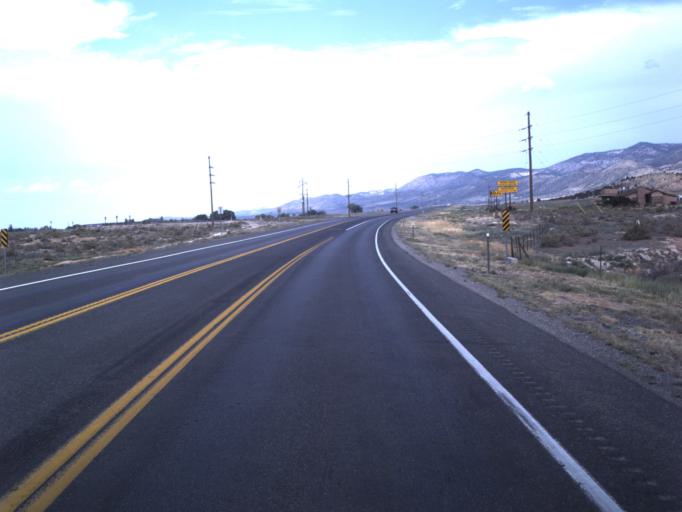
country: US
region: Utah
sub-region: Sanpete County
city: Gunnison
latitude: 39.2072
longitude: -111.8483
